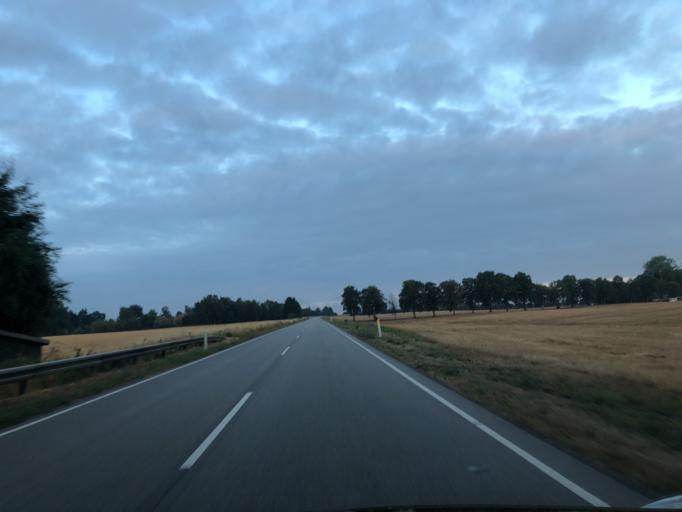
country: DK
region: Zealand
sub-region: Soro Kommune
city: Dianalund
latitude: 55.4826
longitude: 11.4988
